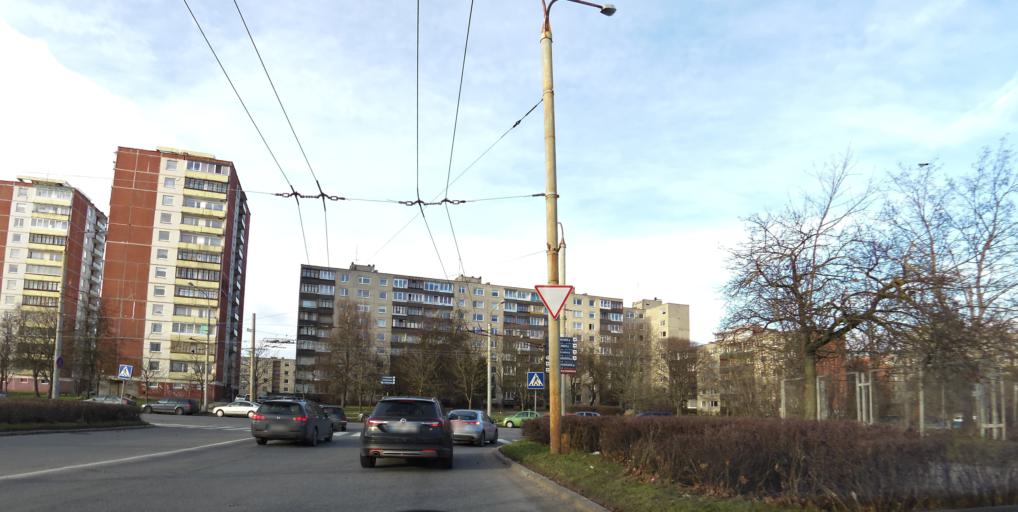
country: LT
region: Vilnius County
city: Justiniskes
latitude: 54.6941
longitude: 25.2165
